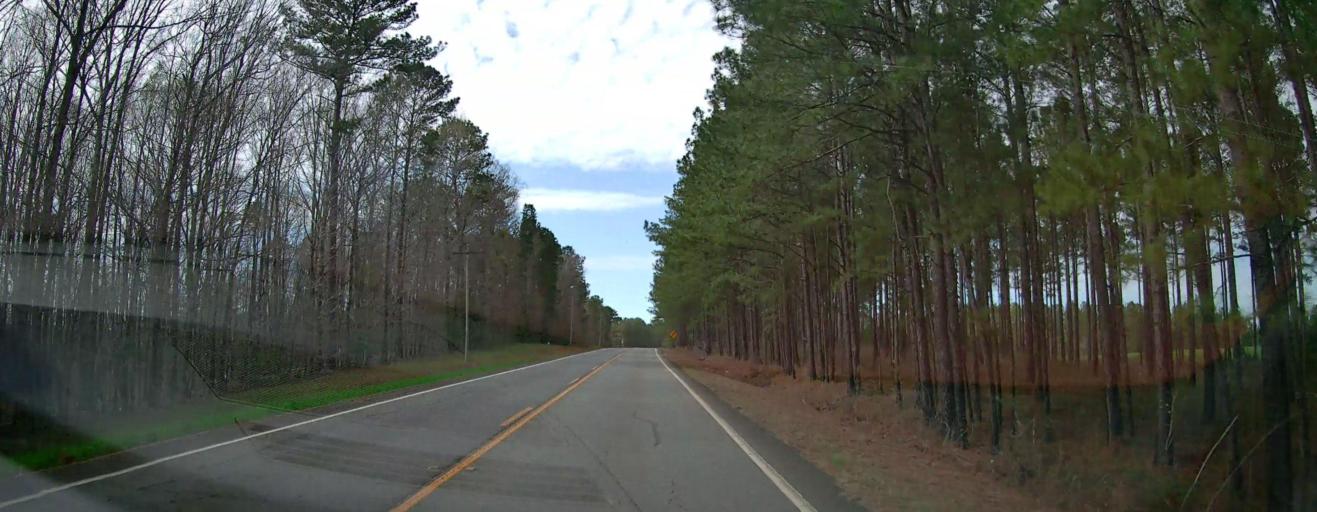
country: US
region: Georgia
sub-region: Jones County
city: Gray
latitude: 33.0029
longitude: -83.6991
